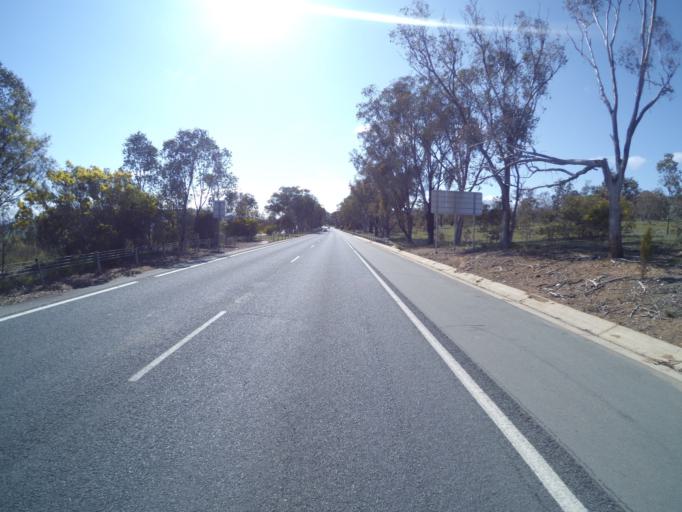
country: AU
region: Australian Capital Territory
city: Kaleen
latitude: -35.2217
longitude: 149.1749
